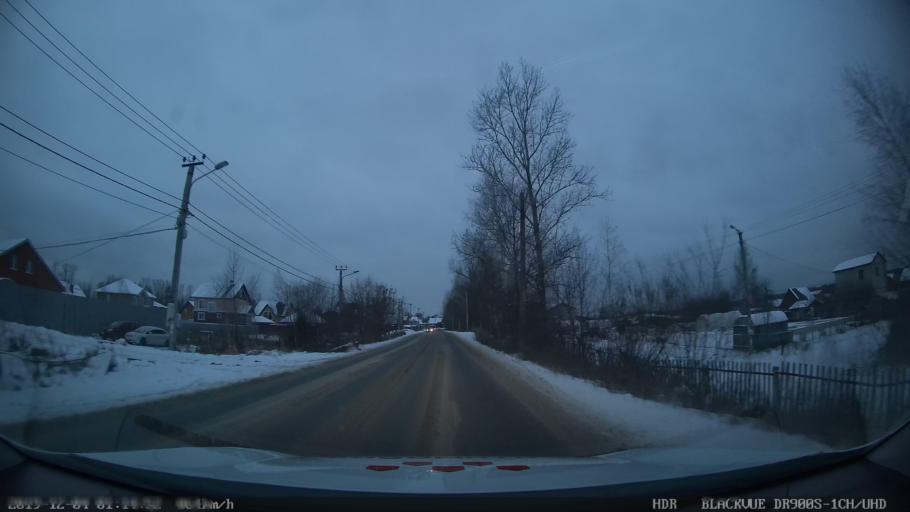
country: RU
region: Tatarstan
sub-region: Gorod Kazan'
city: Kazan
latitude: 55.8764
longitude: 49.1198
